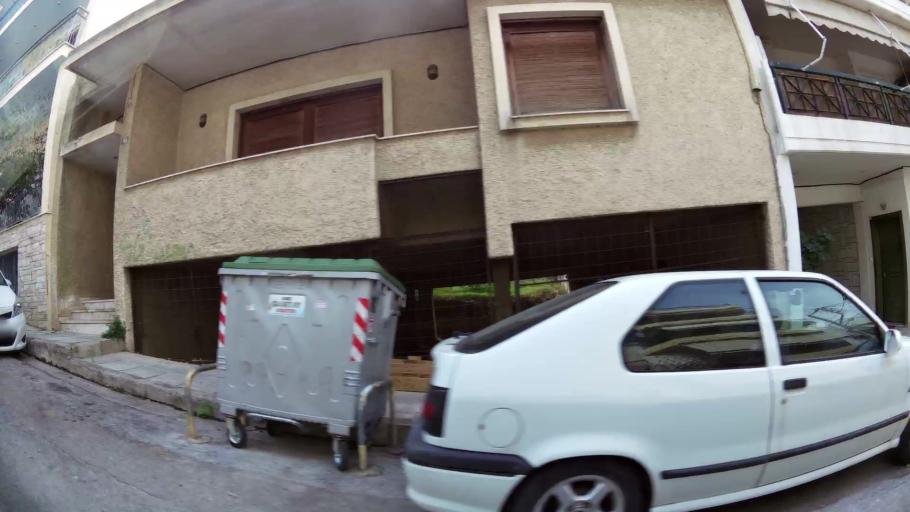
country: GR
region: Attica
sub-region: Nomarchia Athinas
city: Galatsi
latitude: 38.0123
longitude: 23.7575
